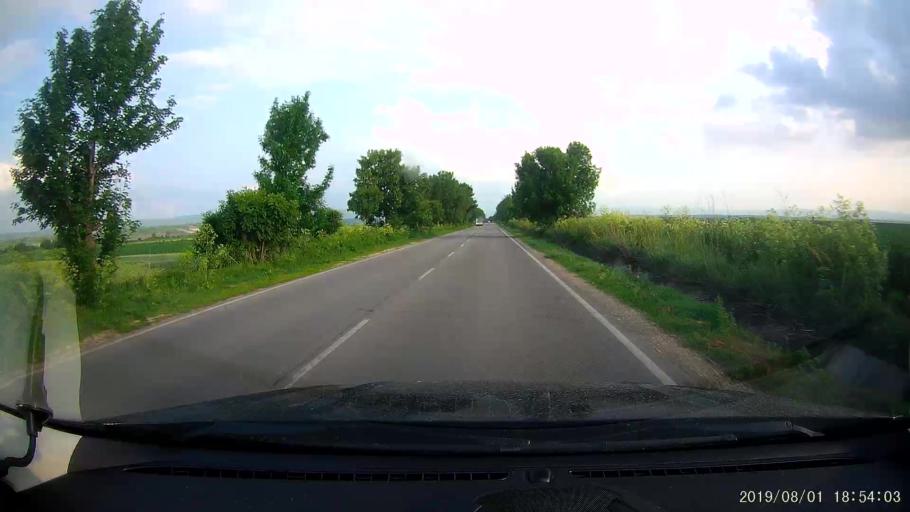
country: BG
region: Shumen
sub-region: Obshtina Shumen
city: Shumen
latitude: 43.2082
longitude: 26.9992
